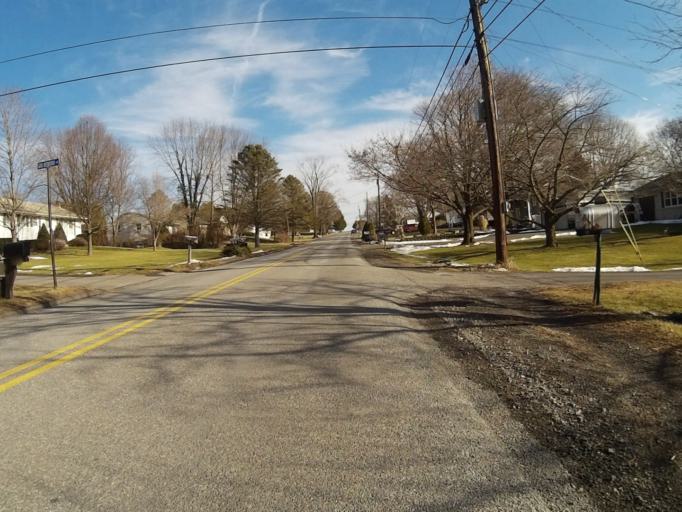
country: US
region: Pennsylvania
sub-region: Centre County
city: Houserville
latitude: 40.8736
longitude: -77.8546
